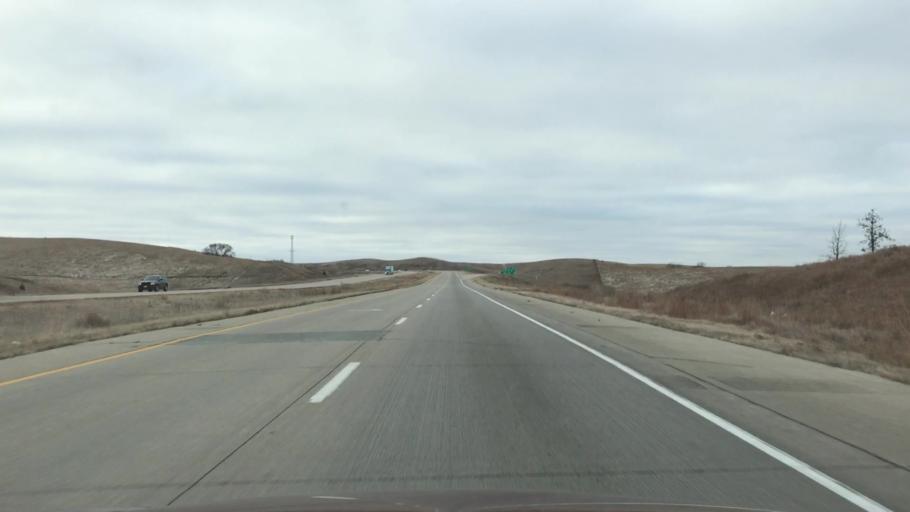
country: US
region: Iowa
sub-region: Woodbury County
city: Sioux City
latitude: 42.5267
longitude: -96.3393
